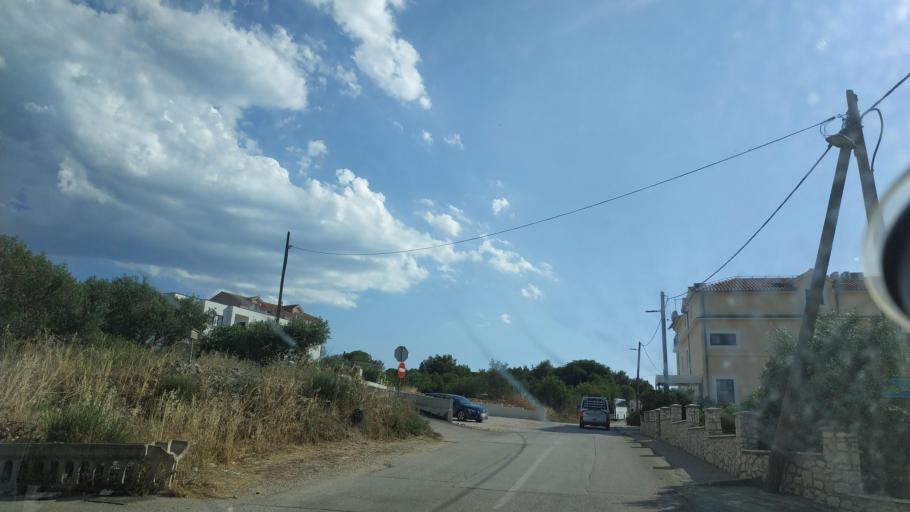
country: HR
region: Splitsko-Dalmatinska
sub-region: Grad Trogir
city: Trogir
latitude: 43.4909
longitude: 16.2553
